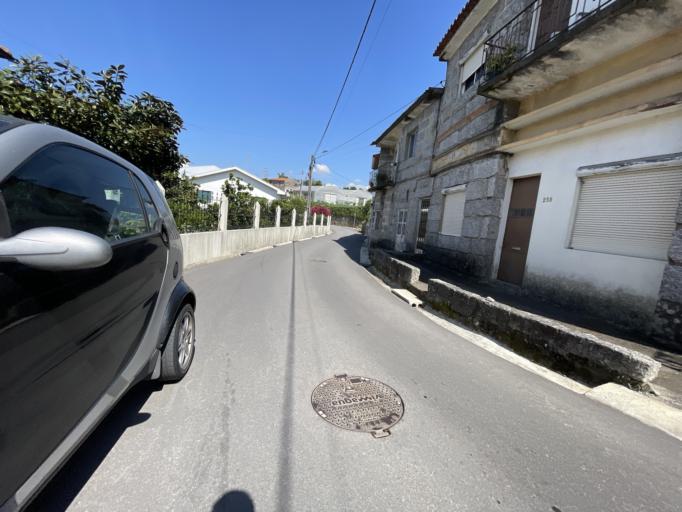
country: PT
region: Braga
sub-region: Guimaraes
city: Guimaraes
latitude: 41.4379
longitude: -8.2869
